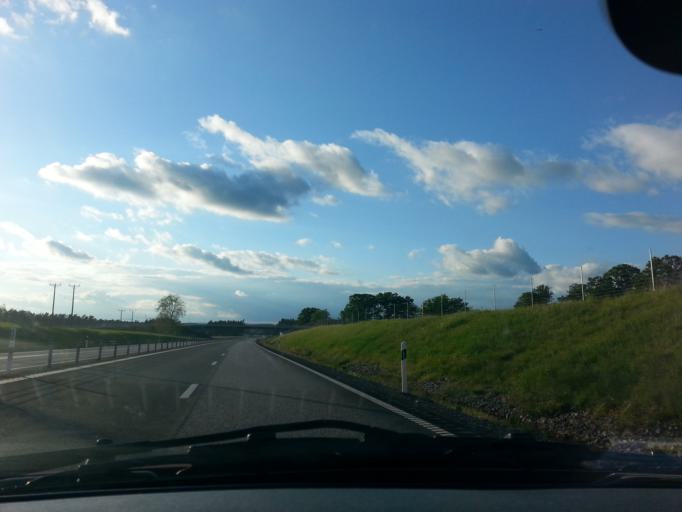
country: SE
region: Joenkoeping
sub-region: Gislaveds Kommun
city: Gislaved
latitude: 57.3010
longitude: 13.5831
